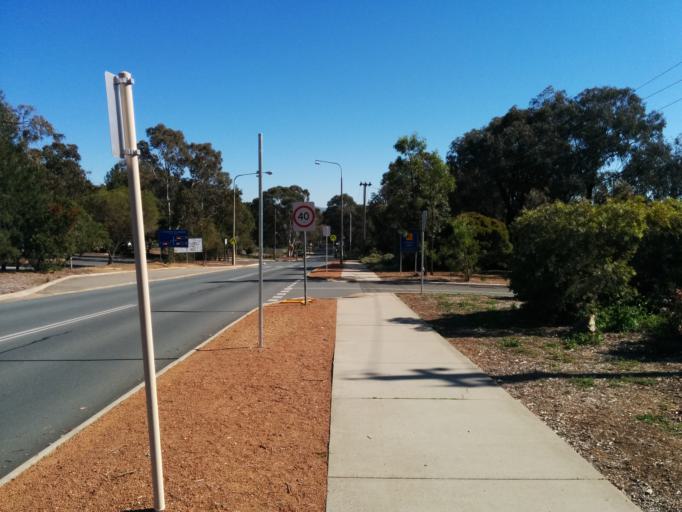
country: AU
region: Australian Capital Territory
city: Macquarie
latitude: -35.2419
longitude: 149.0853
